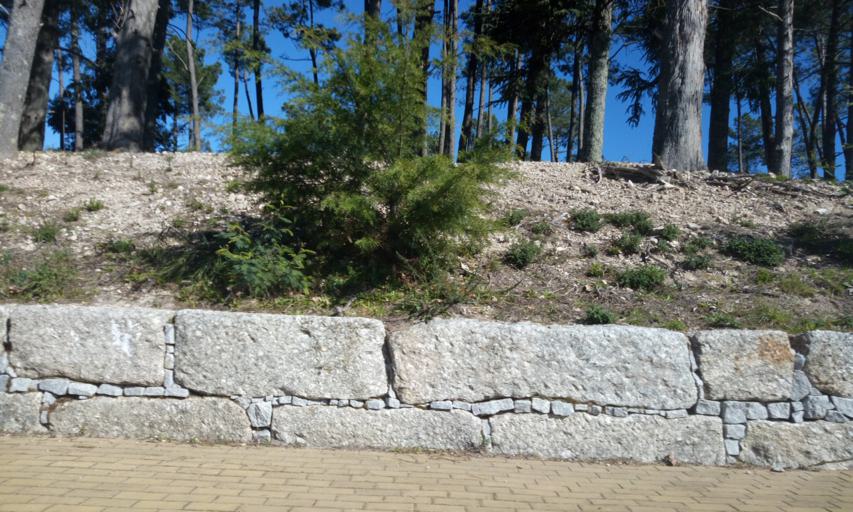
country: PT
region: Guarda
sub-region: Manteigas
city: Manteigas
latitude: 40.4889
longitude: -7.5916
